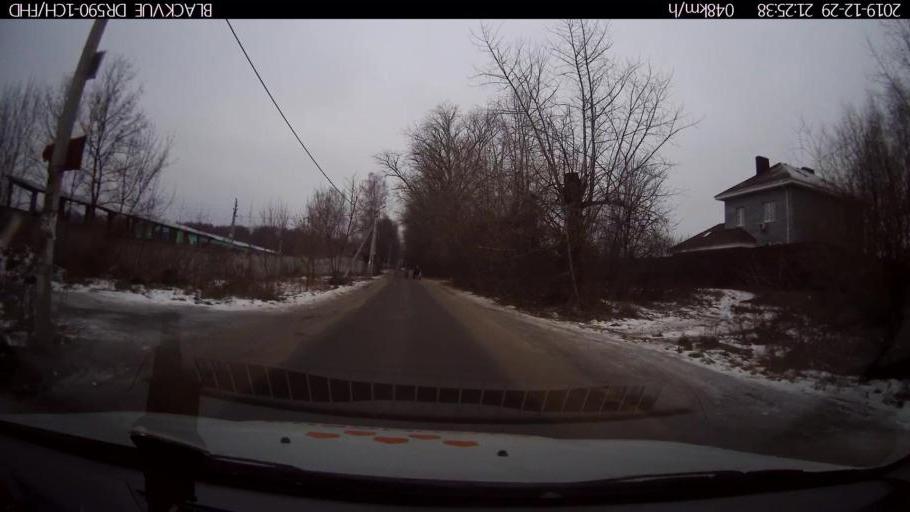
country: RU
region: Nizjnij Novgorod
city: Afonino
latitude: 56.2215
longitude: 44.0382
